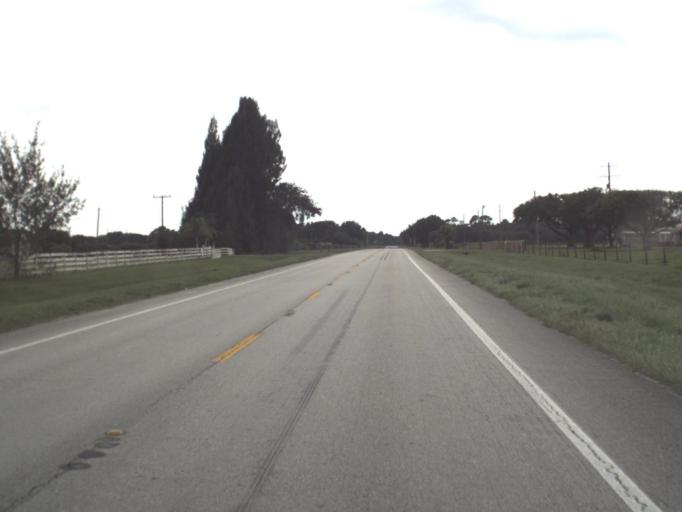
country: US
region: Florida
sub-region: Okeechobee County
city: Cypress Quarters
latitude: 27.3811
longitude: -80.8170
